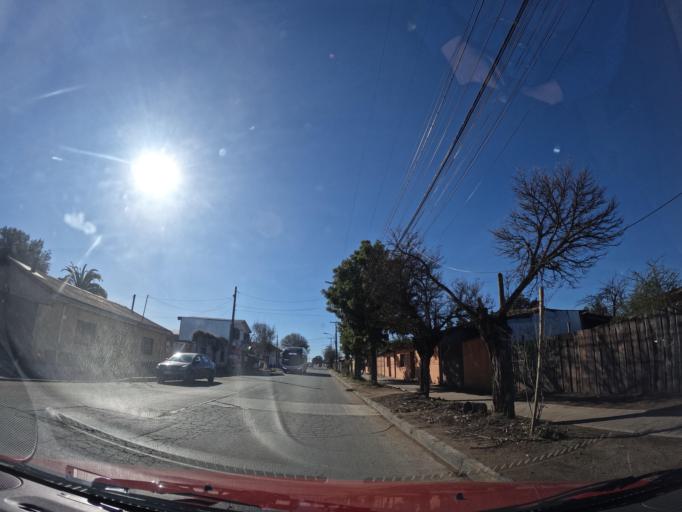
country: CL
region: Maule
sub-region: Provincia de Cauquenes
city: Cauquenes
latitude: -35.9837
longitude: -72.3174
